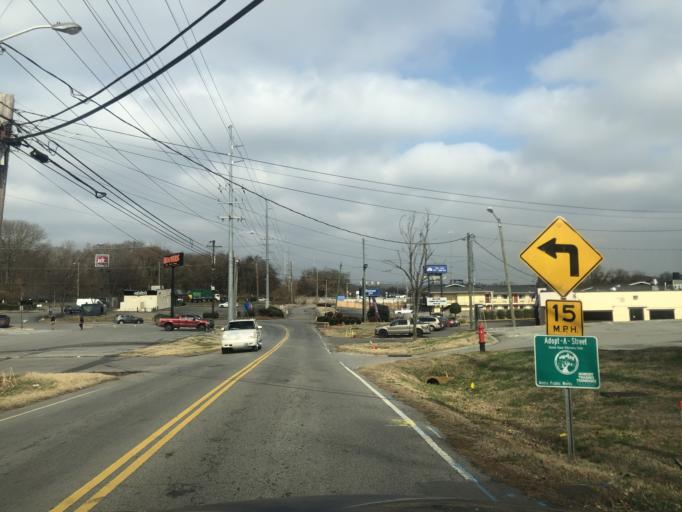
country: US
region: Tennessee
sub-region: Davidson County
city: Oak Hill
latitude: 36.0837
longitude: -86.7020
